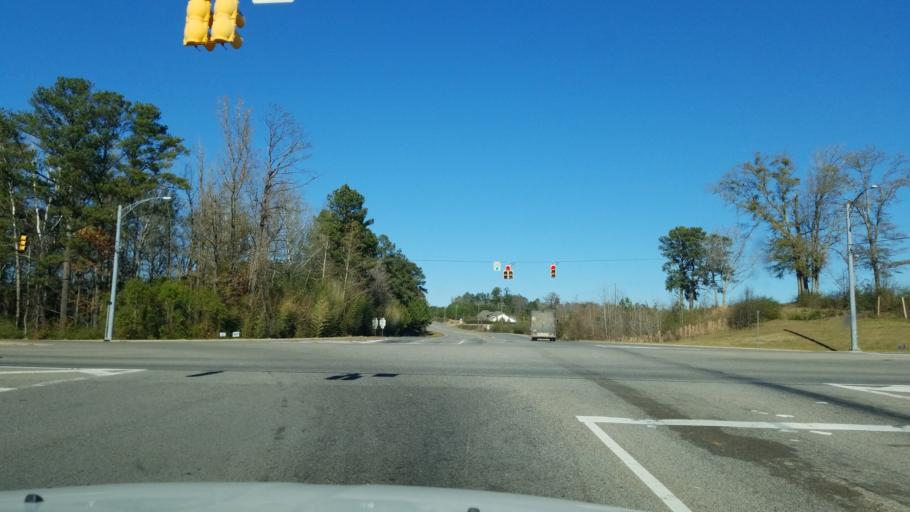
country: US
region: Alabama
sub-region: Tuscaloosa County
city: Northport
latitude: 33.2340
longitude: -87.6386
